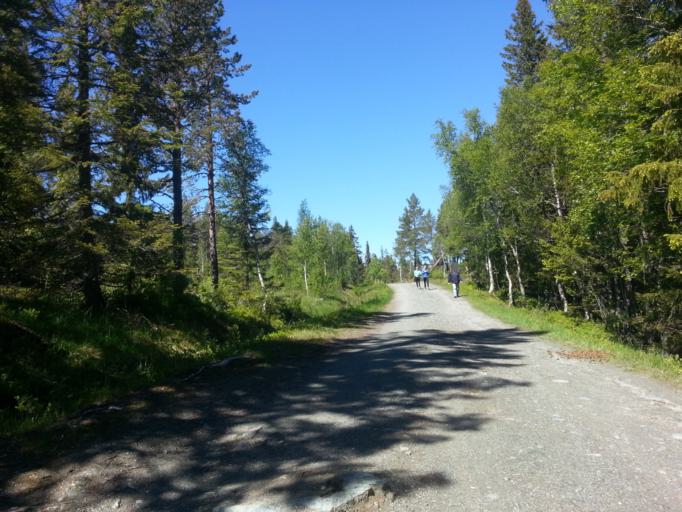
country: NO
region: Sor-Trondelag
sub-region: Trondheim
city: Trondheim
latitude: 63.4089
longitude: 10.2889
